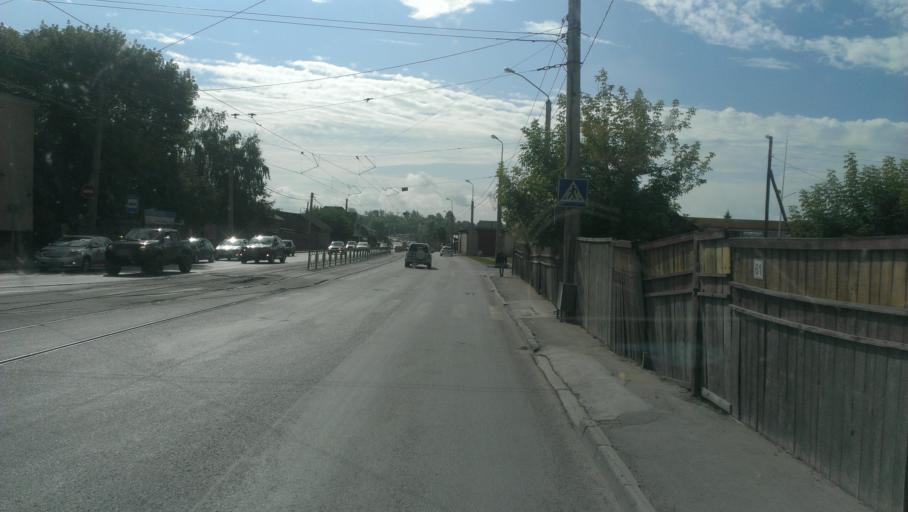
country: RU
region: Altai Krai
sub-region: Gorod Barnaulskiy
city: Barnaul
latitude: 53.3441
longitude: 83.7340
